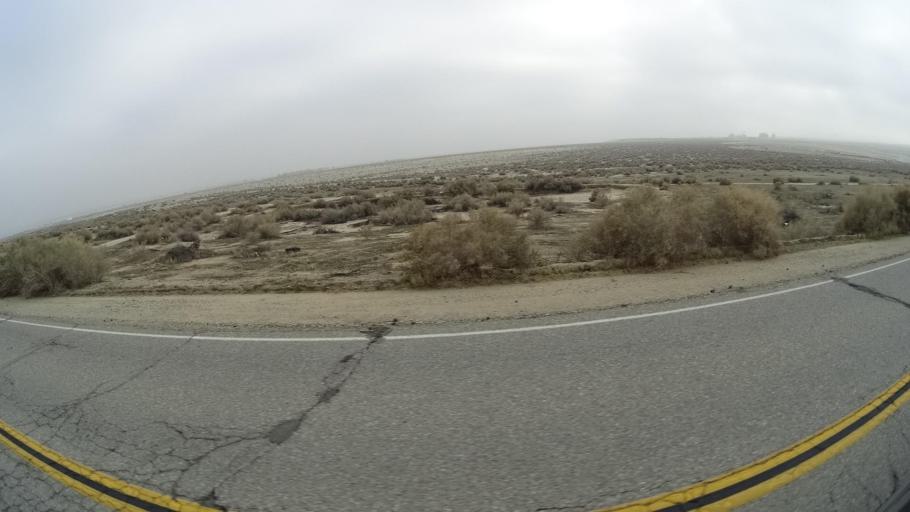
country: US
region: California
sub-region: Kern County
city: South Taft
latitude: 35.1301
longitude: -119.3892
